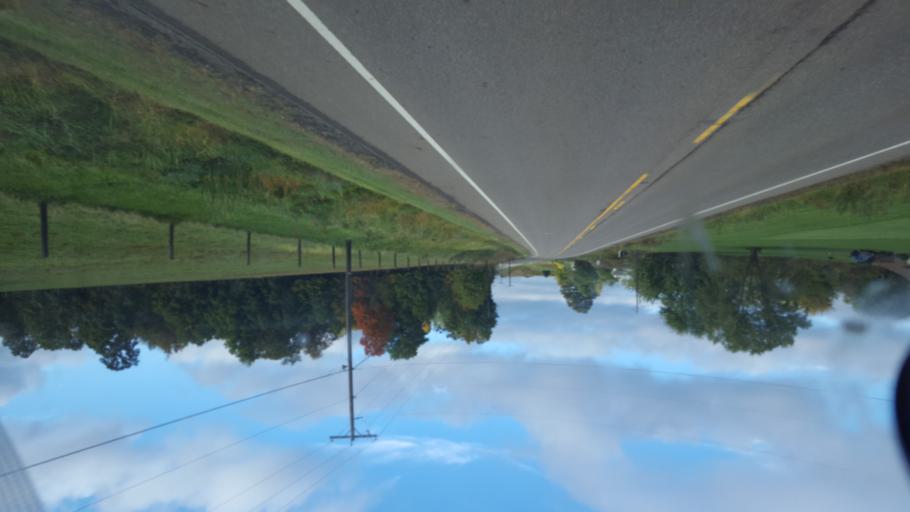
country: US
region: Ohio
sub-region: Knox County
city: Fredericktown
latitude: 40.5477
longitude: -82.5406
